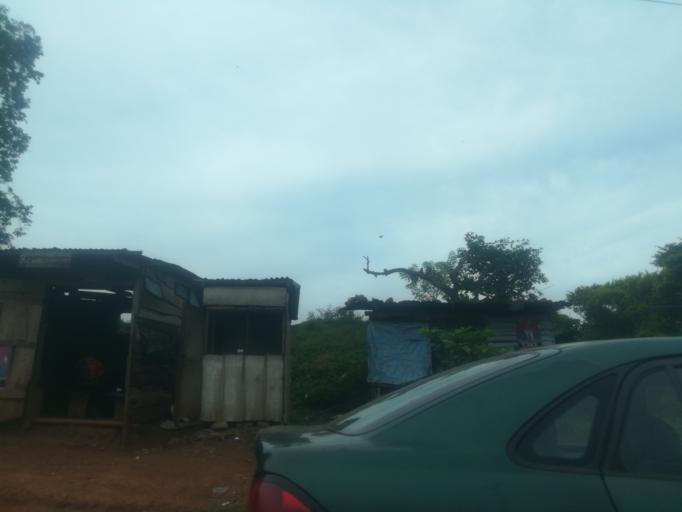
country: NG
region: Oyo
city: Ibadan
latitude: 7.3758
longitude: 3.9301
